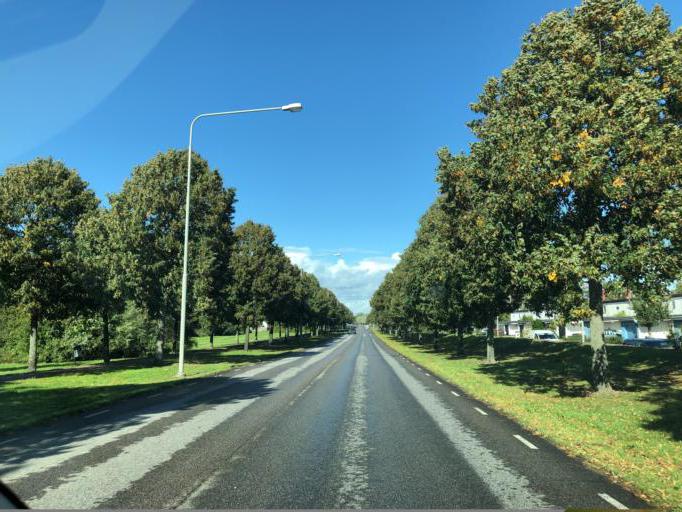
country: SE
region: Skane
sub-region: Landskrona
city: Landskrona
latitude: 55.8917
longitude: 12.8288
